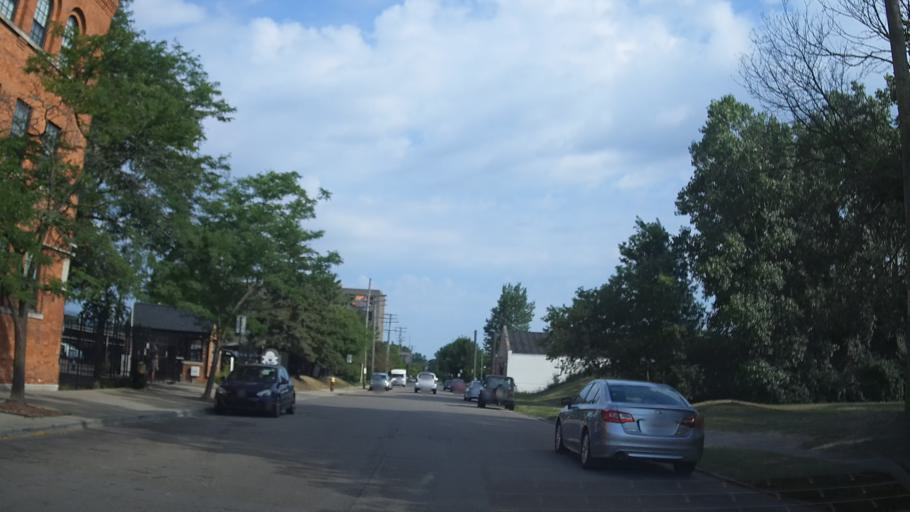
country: US
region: Michigan
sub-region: Wayne County
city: Detroit
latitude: 42.3460
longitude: -83.0067
